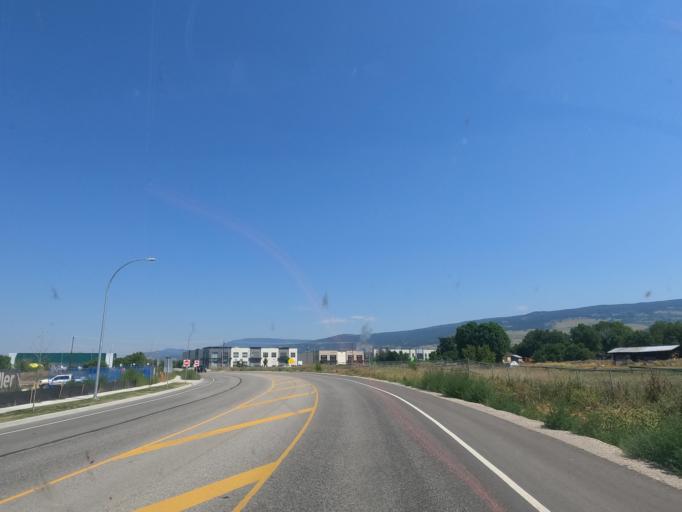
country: CA
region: British Columbia
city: Kelowna
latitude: 49.9164
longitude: -119.3846
